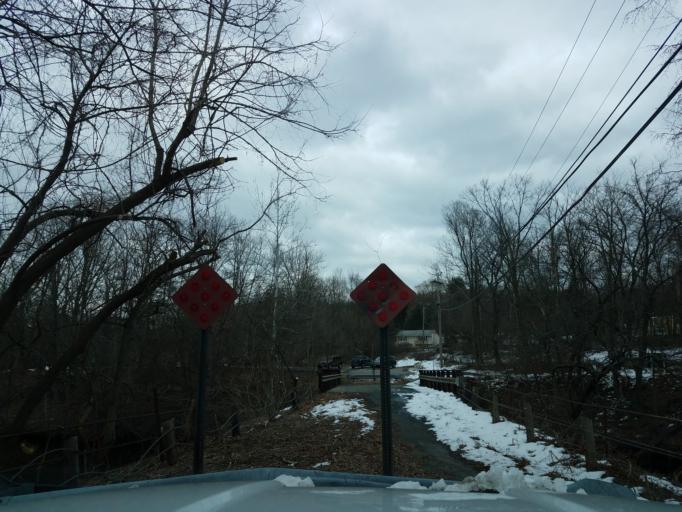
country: US
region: Connecticut
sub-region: Litchfield County
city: New Milford
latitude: 41.5406
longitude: -73.4129
